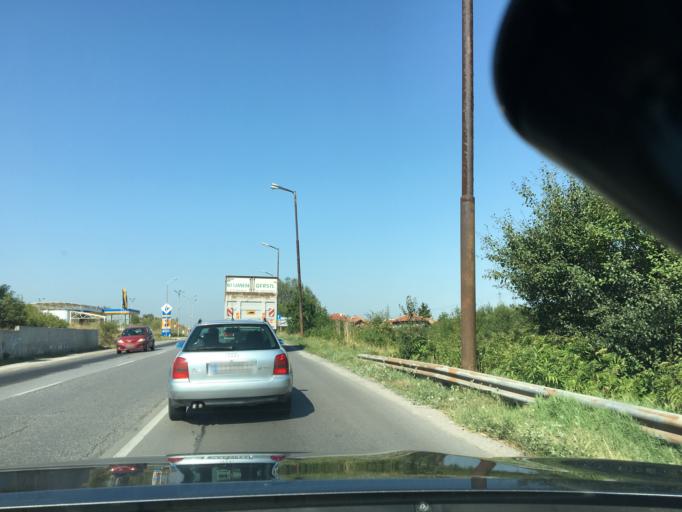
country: BG
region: Pernik
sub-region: Obshtina Pernik
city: Pernik
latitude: 42.6014
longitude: 23.1321
